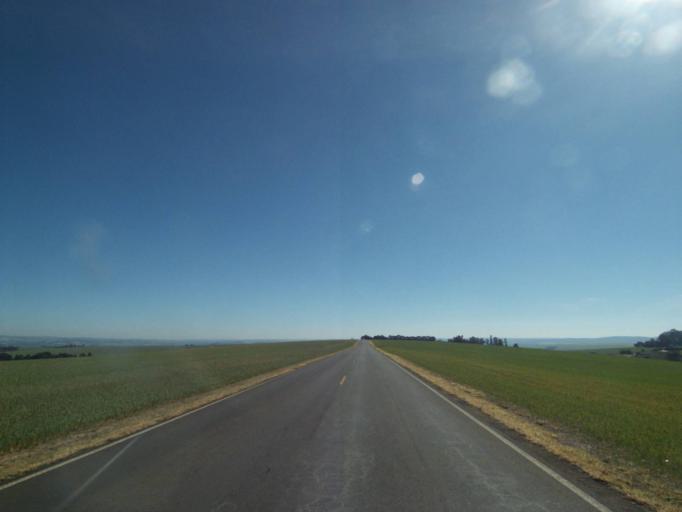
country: BR
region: Parana
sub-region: Tibagi
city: Tibagi
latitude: -24.5286
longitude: -50.3213
